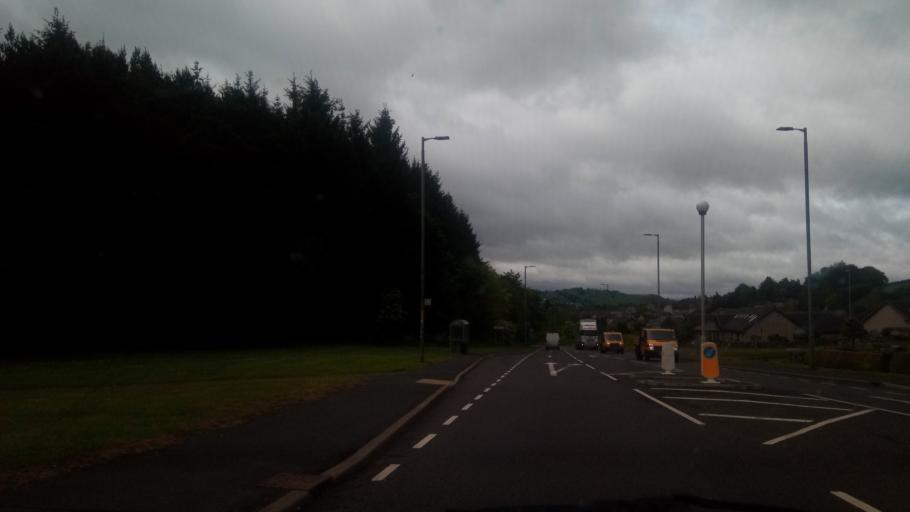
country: GB
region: Scotland
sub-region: The Scottish Borders
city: Hawick
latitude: 55.4383
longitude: -2.7777
